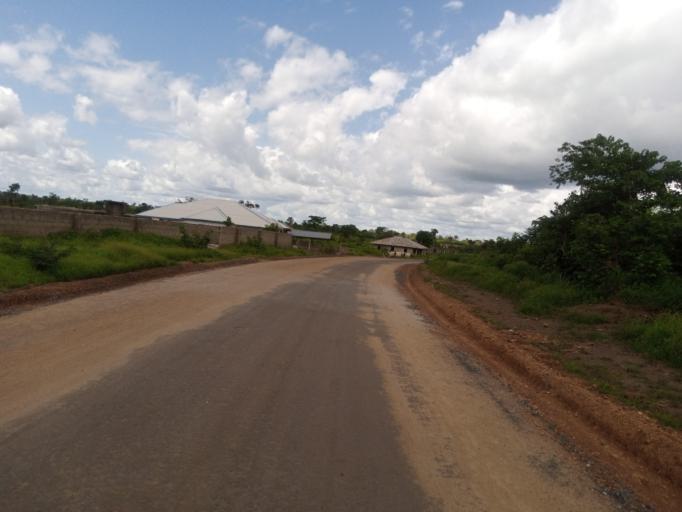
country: SL
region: Northern Province
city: Port Loko
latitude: 8.7770
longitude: -12.7681
